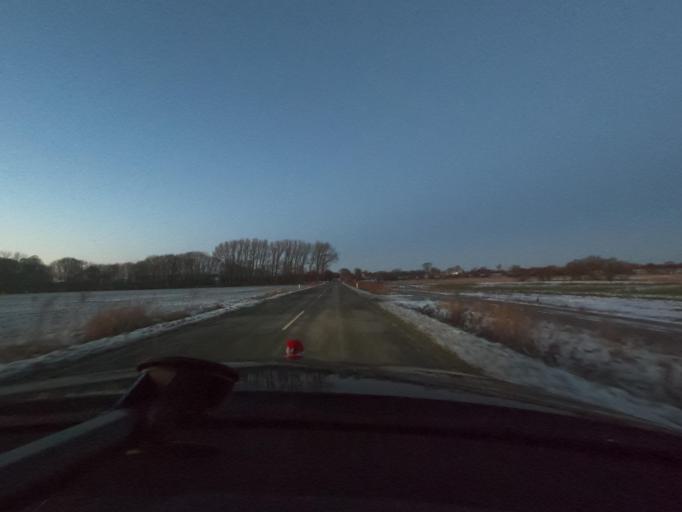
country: DK
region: South Denmark
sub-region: Sonderborg Kommune
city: Horuphav
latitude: 54.8724
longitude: 9.9957
